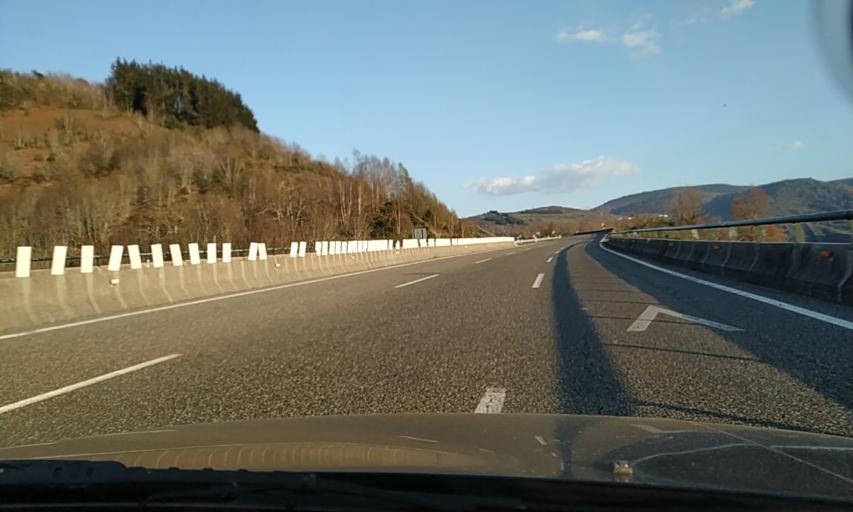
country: ES
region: Galicia
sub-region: Provincia de Lugo
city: San Roman
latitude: 42.7530
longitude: -7.0670
